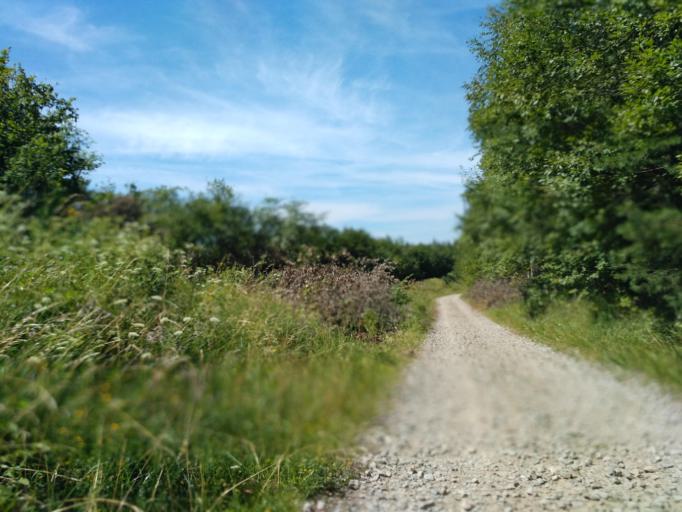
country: PL
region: Subcarpathian Voivodeship
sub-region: Powiat sanocki
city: Bukowsko
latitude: 49.4864
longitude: 22.0928
